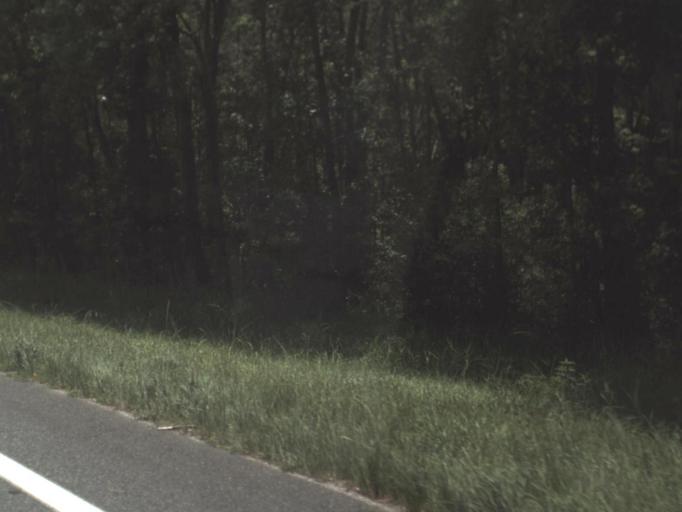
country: US
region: Florida
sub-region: Columbia County
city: Five Points
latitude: 30.2355
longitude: -82.6679
